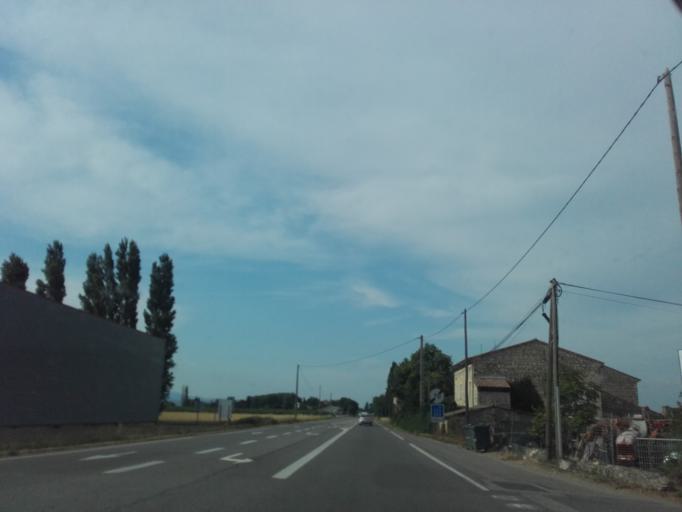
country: FR
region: Rhone-Alpes
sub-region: Departement de la Drome
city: Livron-sur-Drome
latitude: 44.7830
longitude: 4.8492
